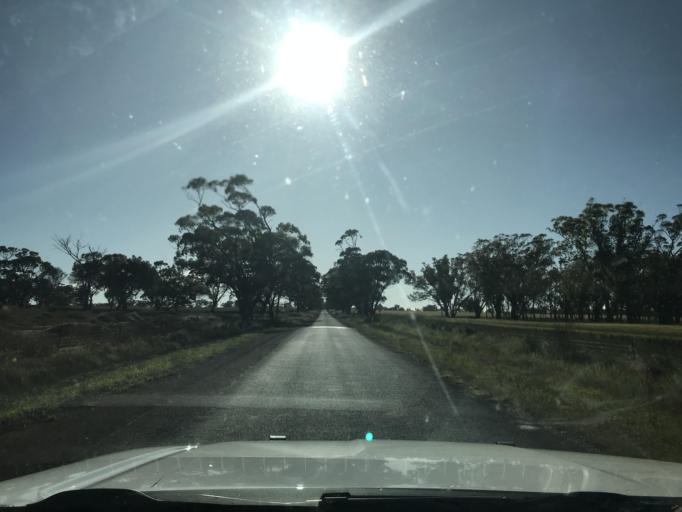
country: AU
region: Victoria
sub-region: Horsham
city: Horsham
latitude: -36.6905
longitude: 141.5283
